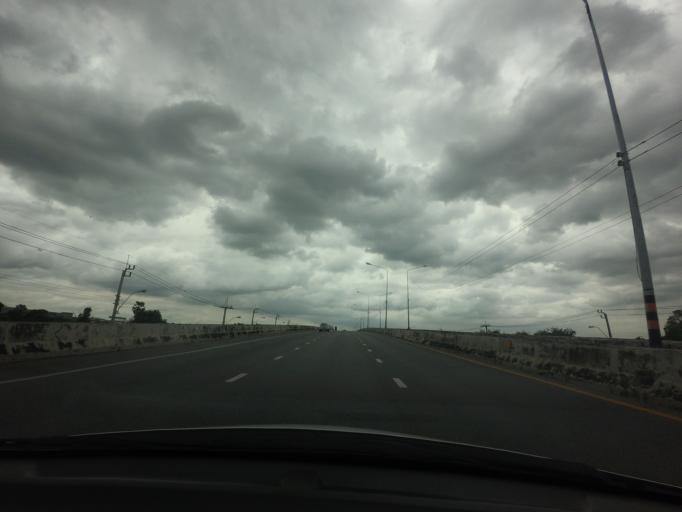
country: TH
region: Bangkok
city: Saphan Sung
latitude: 13.7556
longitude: 100.7377
